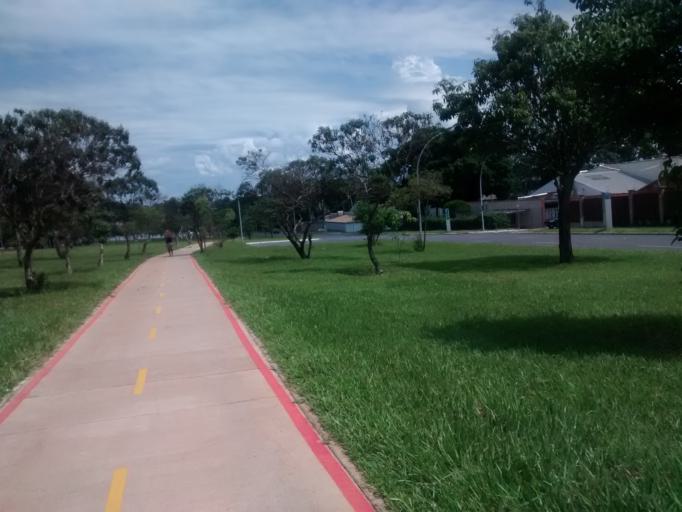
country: BR
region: Federal District
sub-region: Brasilia
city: Brasilia
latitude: -15.7607
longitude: -47.8952
